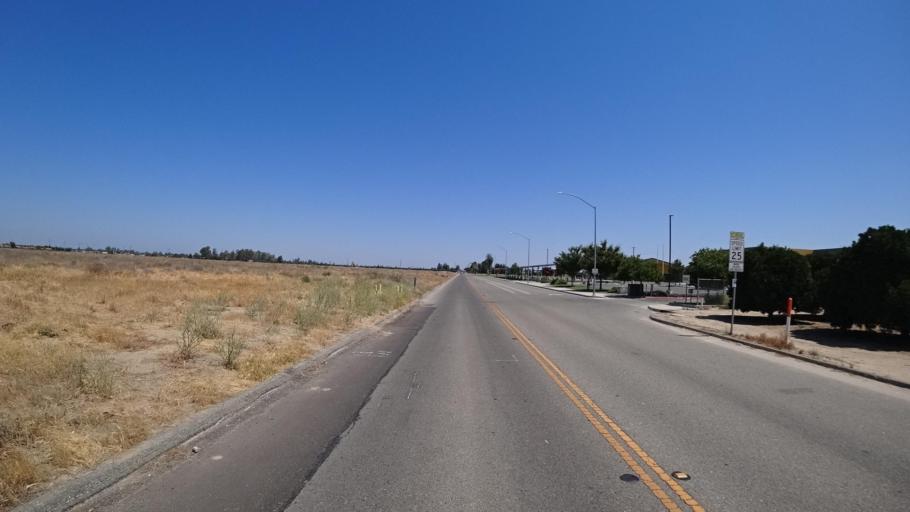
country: US
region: California
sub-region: Fresno County
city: Sunnyside
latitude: 36.7093
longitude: -119.6731
